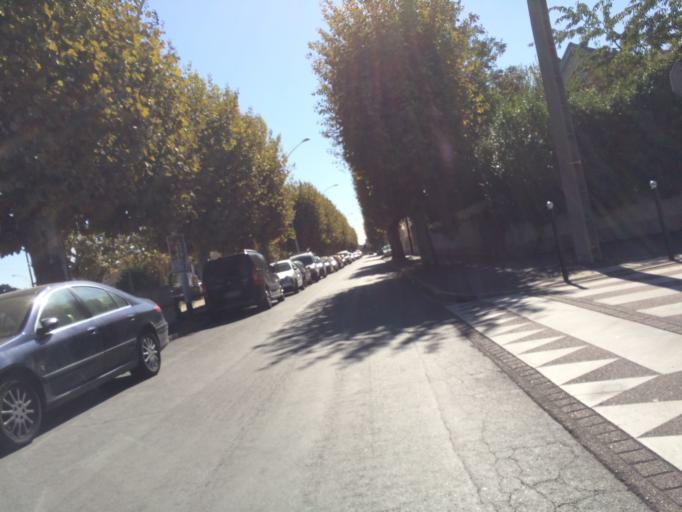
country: FR
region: Ile-de-France
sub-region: Departement de l'Essonne
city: Savigny-sur-Orge
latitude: 48.6901
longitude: 2.3571
